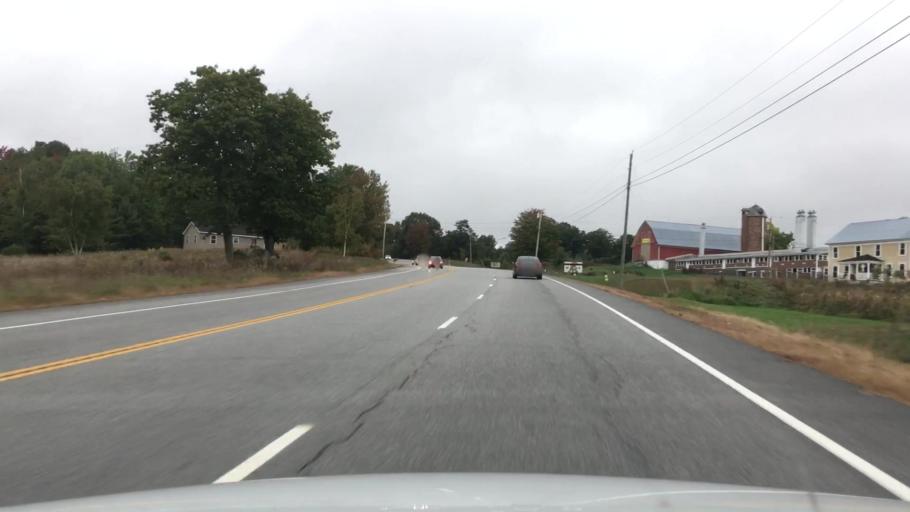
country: US
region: Maine
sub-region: Androscoggin County
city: Poland
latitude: 44.0830
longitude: -70.4185
